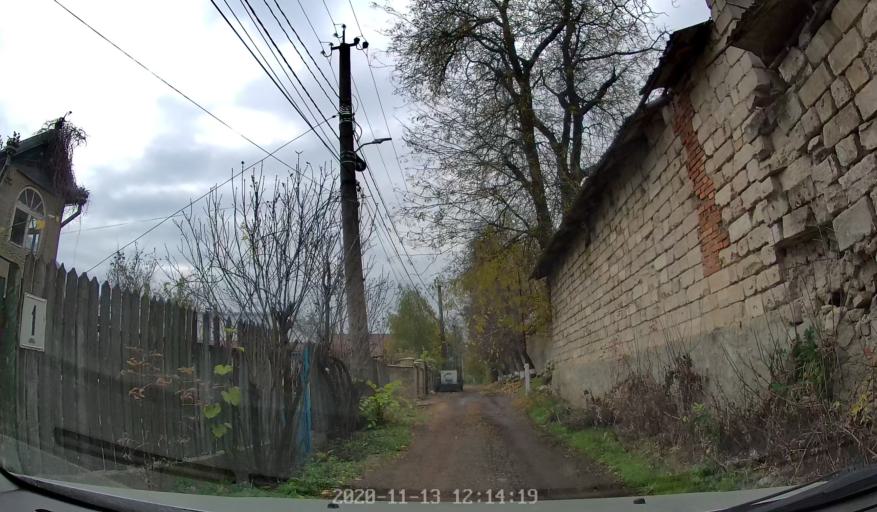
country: MD
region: Chisinau
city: Chisinau
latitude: 46.9529
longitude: 28.8381
